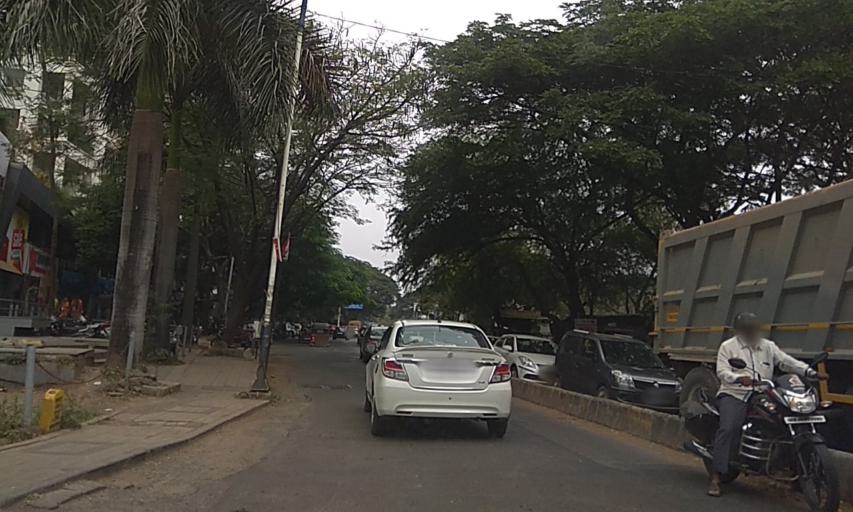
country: IN
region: Maharashtra
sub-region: Pune Division
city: Khadki
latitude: 18.5652
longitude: 73.8075
